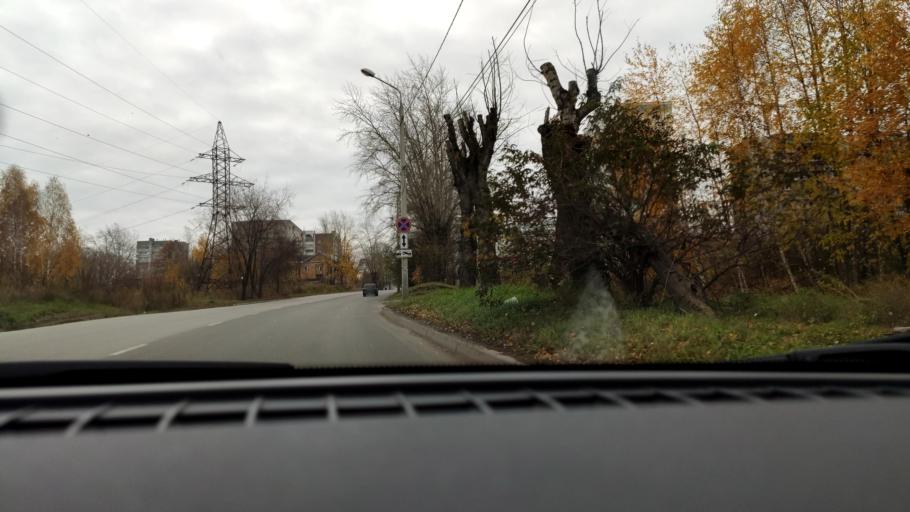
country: RU
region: Perm
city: Perm
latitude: 58.0703
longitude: 56.3532
